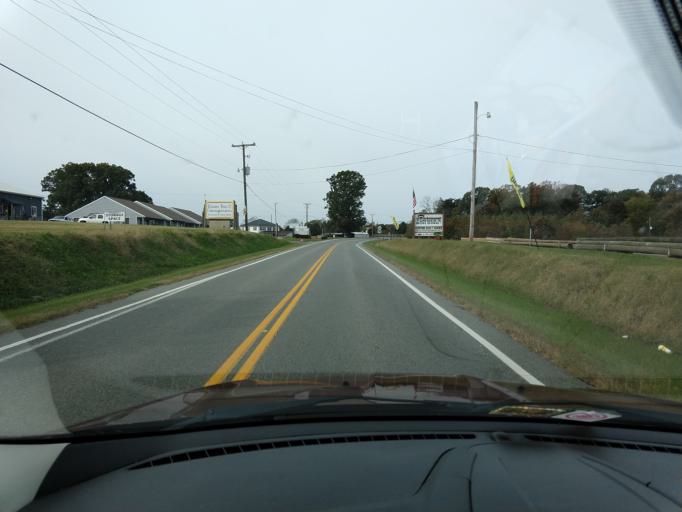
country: US
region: Virginia
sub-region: Franklin County
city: Union Hall
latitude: 36.9934
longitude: -79.6836
